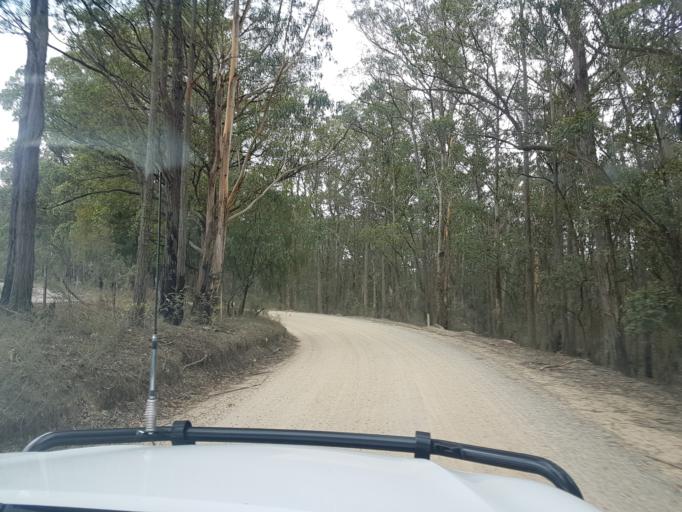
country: AU
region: Victoria
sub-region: East Gippsland
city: Bairnsdale
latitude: -37.6887
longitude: 147.5615
